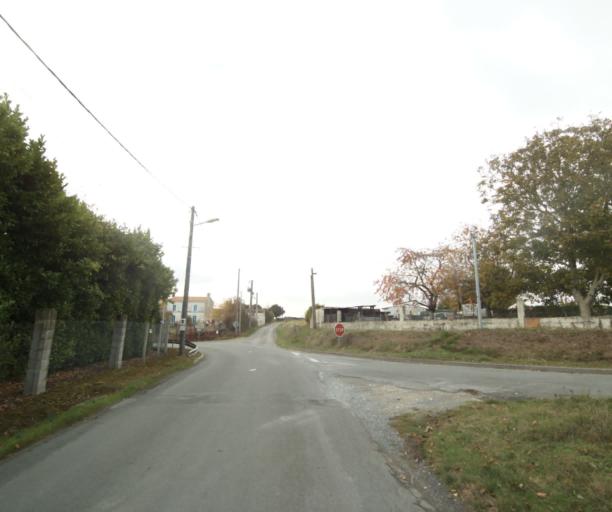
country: FR
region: Poitou-Charentes
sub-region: Departement de la Charente-Maritime
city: Saint-Georges-des-Coteaux
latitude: 45.7682
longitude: -0.7194
